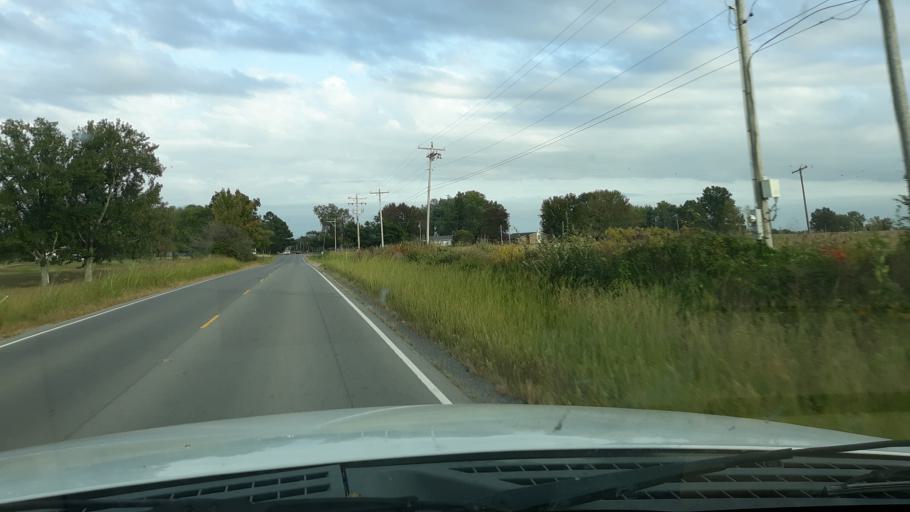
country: US
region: Illinois
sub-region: Saline County
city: Eldorado
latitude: 37.8212
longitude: -88.4880
